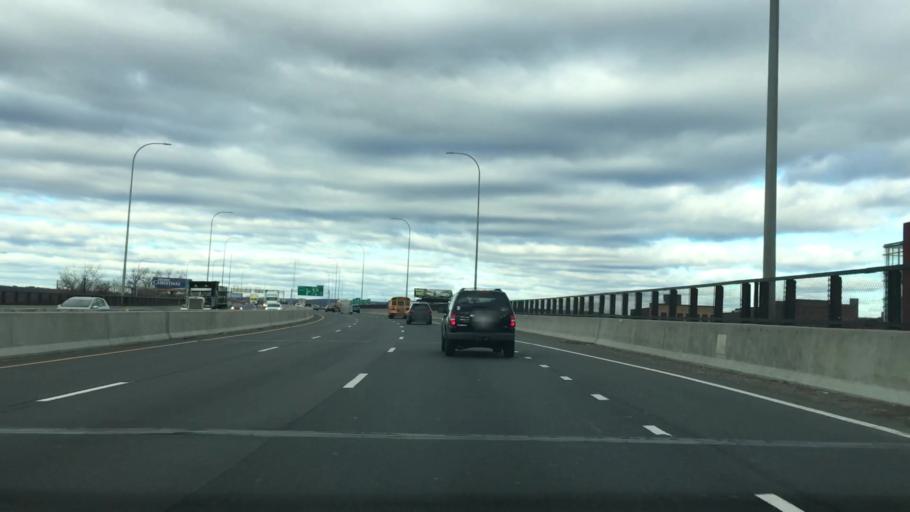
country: US
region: Massachusetts
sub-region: Hampden County
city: Springfield
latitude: 42.1020
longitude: -72.5934
